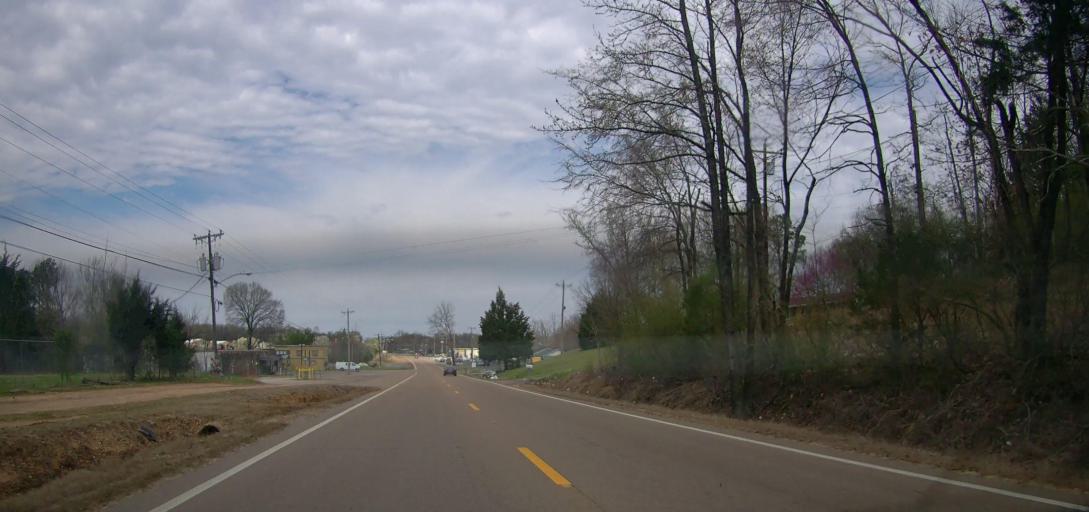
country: US
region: Mississippi
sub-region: De Soto County
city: Olive Branch
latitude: 34.9871
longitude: -89.8622
